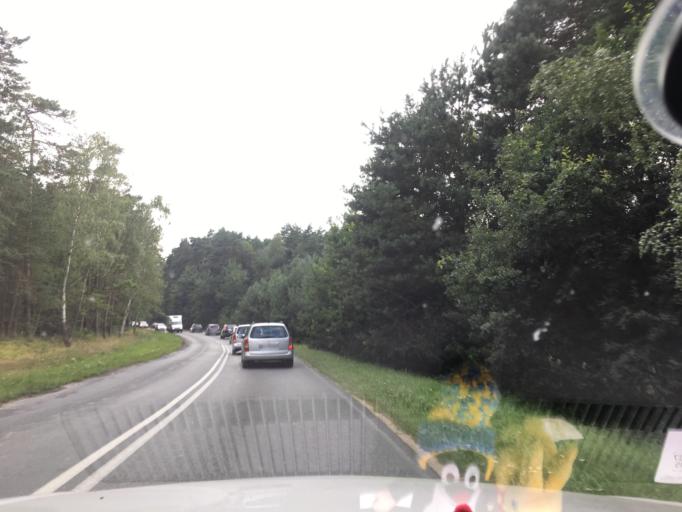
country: PL
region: West Pomeranian Voivodeship
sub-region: Powiat gryficki
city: Pobierowo
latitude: 54.0636
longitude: 14.9616
